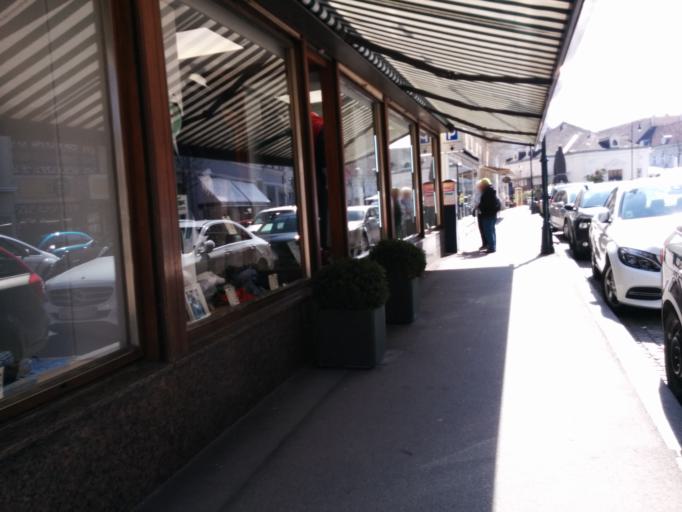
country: AT
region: Lower Austria
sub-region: Politischer Bezirk Baden
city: Baden
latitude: 48.0072
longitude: 16.2323
